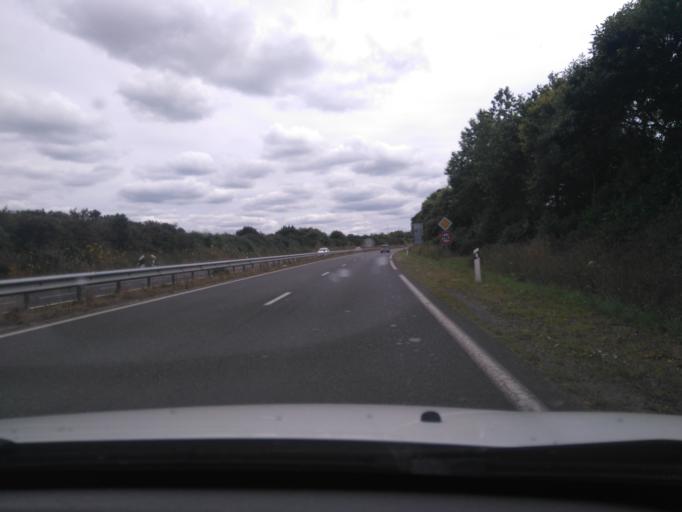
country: FR
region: Brittany
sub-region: Departement des Cotes-d'Armor
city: Cavan
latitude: 48.6802
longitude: -3.3566
